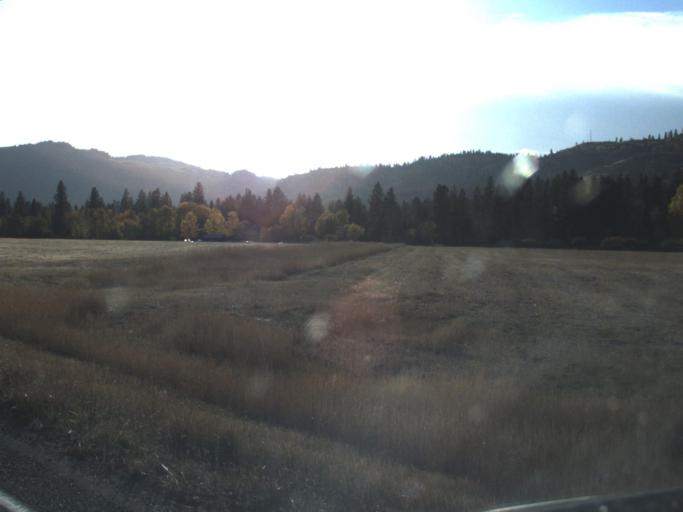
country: CA
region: British Columbia
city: Rossland
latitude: 48.8378
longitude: -117.9044
